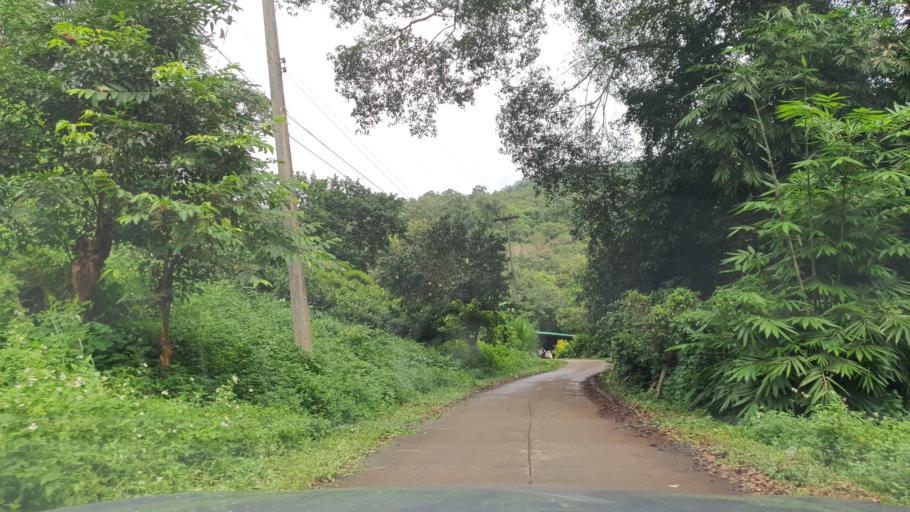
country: TH
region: Chiang Mai
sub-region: Amphoe Chiang Dao
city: Chiang Dao
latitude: 19.2448
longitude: 98.9260
